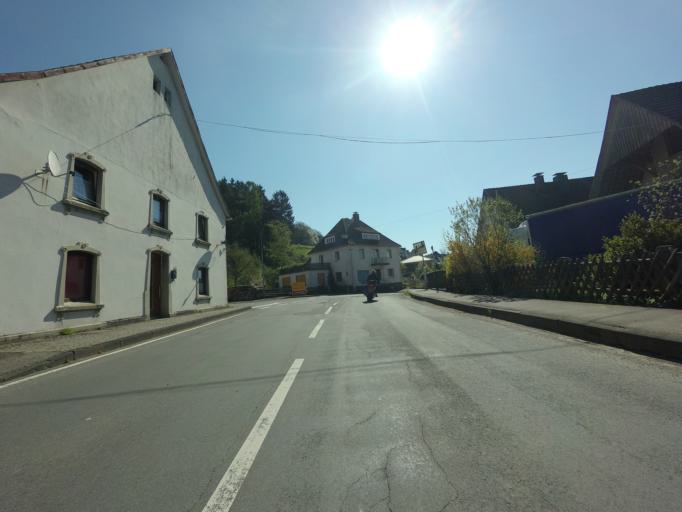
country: DE
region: North Rhine-Westphalia
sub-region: Regierungsbezirk Arnsberg
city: Drolshagen
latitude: 51.0803
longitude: 7.7969
